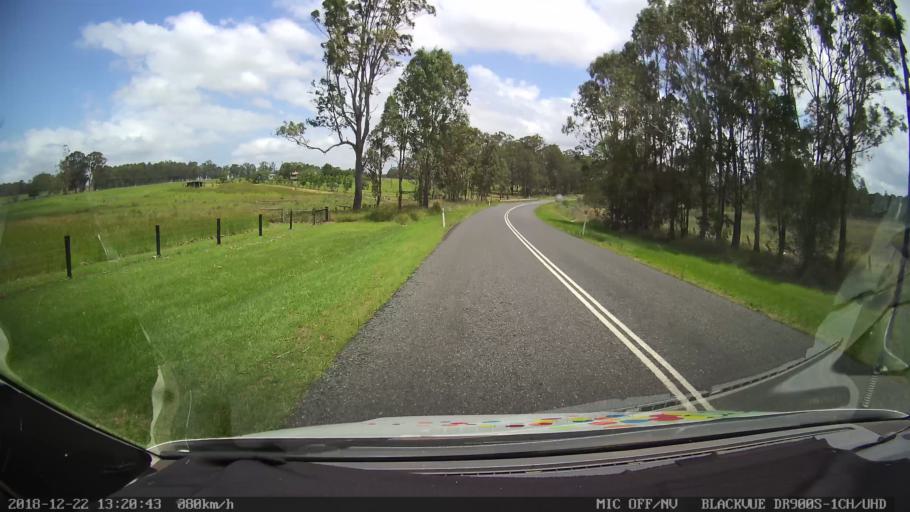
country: AU
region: New South Wales
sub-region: Clarence Valley
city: South Grafton
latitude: -29.7696
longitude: 152.9263
